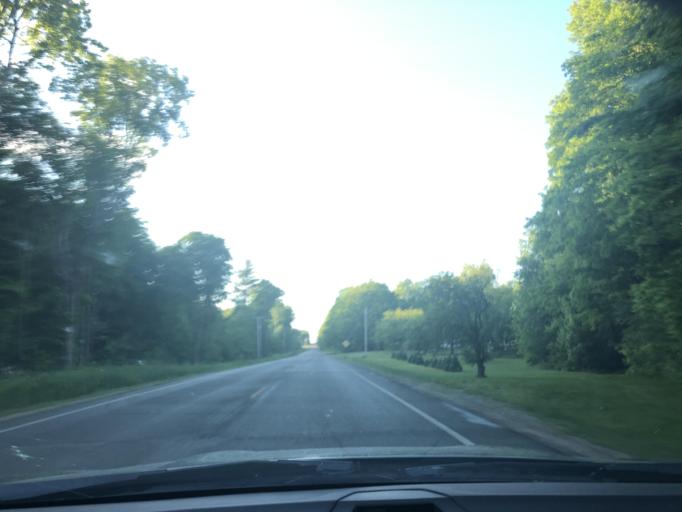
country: US
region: Michigan
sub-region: Missaukee County
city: Lake City
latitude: 44.4588
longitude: -85.0744
